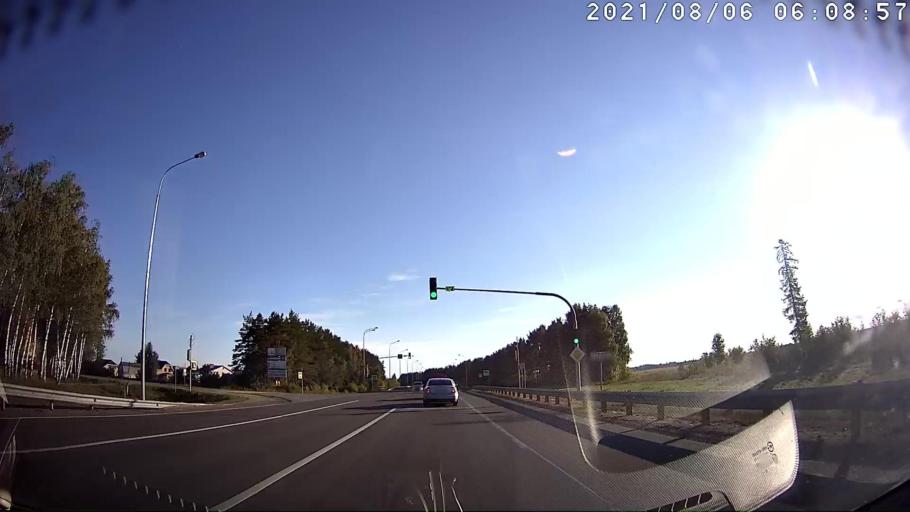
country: RU
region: Mariy-El
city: Pomary
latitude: 55.9197
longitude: 48.3718
